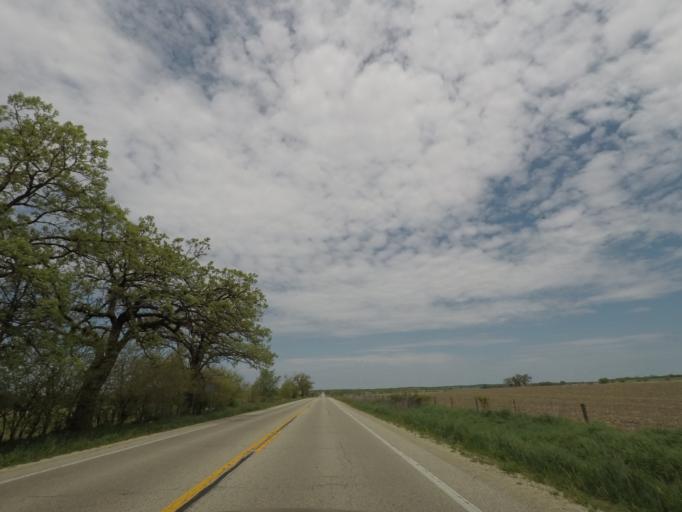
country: US
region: Wisconsin
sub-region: Rock County
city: Evansville
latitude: 42.7396
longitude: -89.2988
